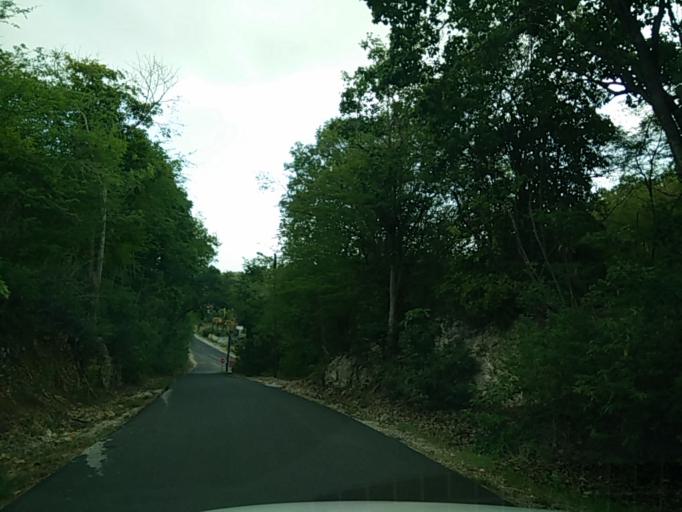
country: GP
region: Guadeloupe
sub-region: Guadeloupe
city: Sainte-Anne
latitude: 16.2197
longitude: -61.4047
